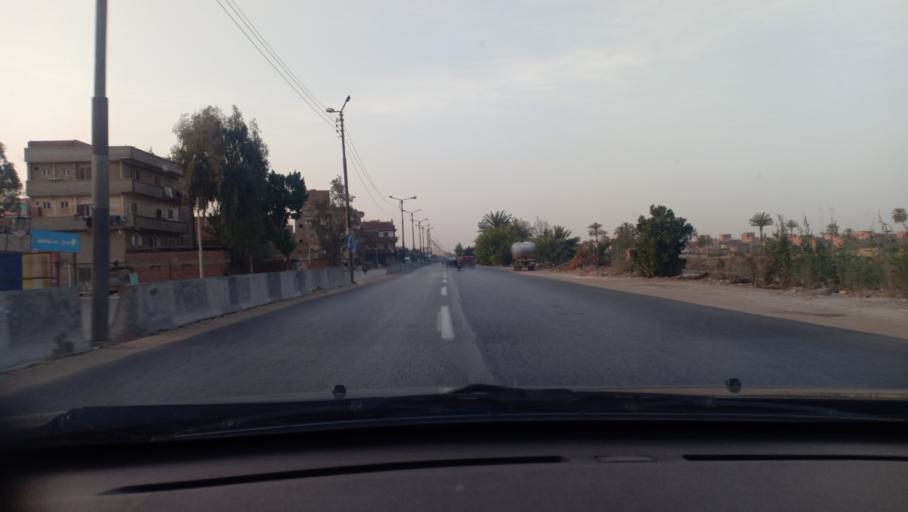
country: EG
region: Muhafazat al Gharbiyah
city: Zifta
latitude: 30.6626
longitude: 31.2849
